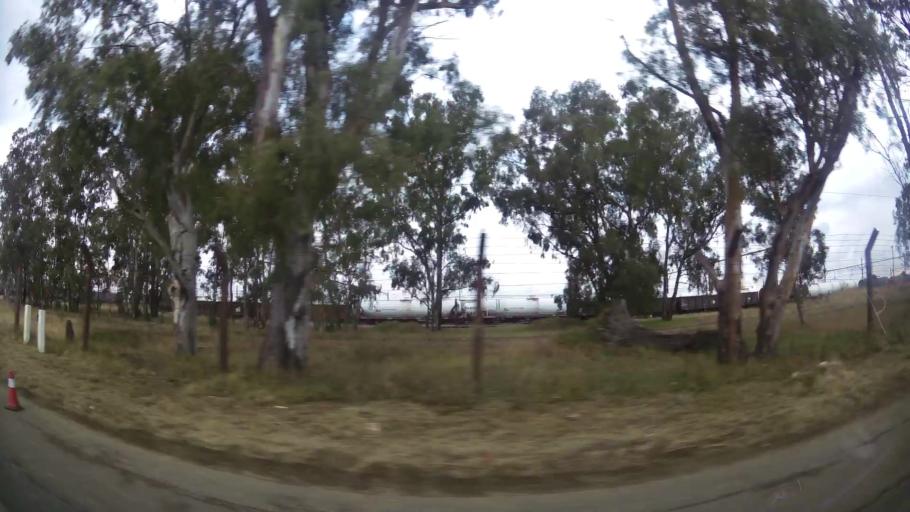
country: ZA
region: Orange Free State
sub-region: Fezile Dabi District Municipality
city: Sasolburg
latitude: -26.8492
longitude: 27.8682
